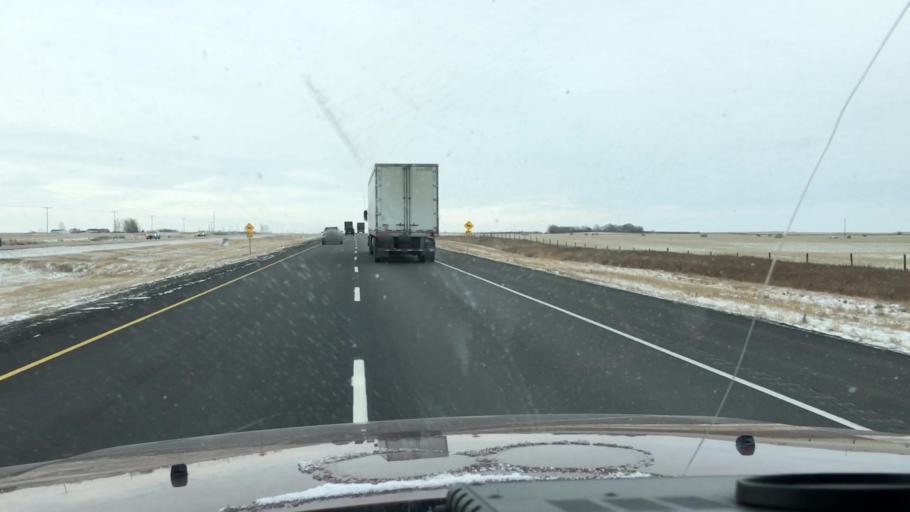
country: CA
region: Saskatchewan
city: Saskatoon
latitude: 51.7933
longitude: -106.4852
